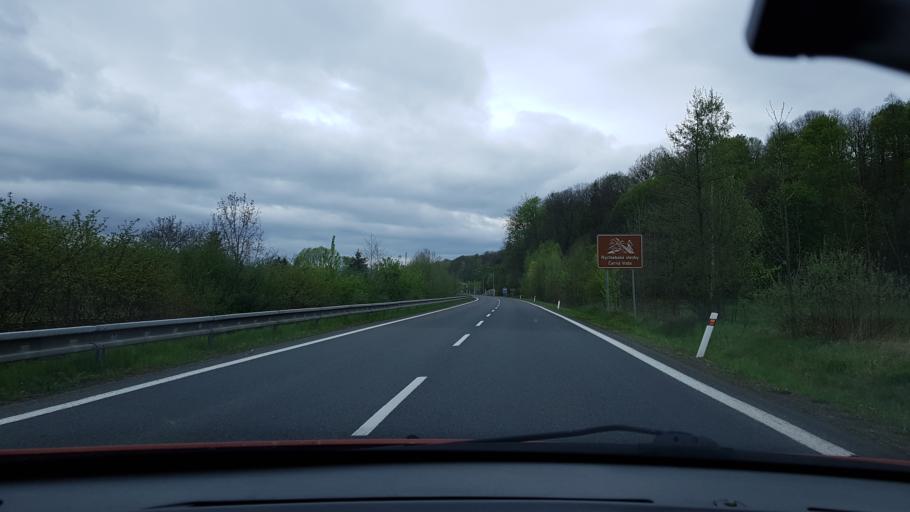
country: CZ
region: Olomoucky
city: Mikulovice
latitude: 50.3056
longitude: 17.3267
